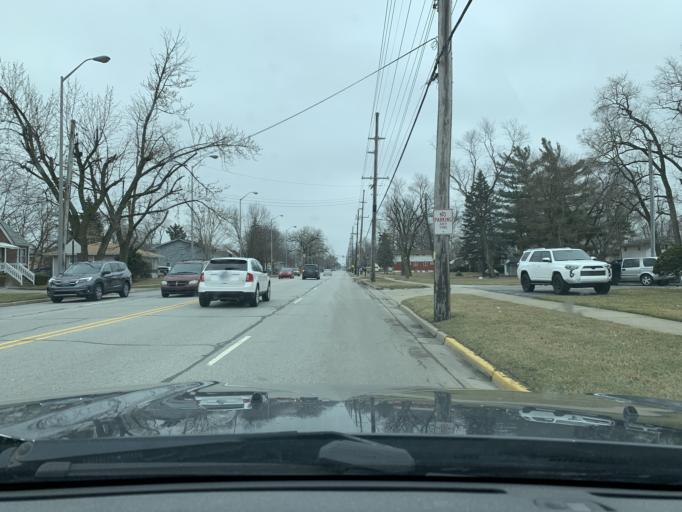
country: US
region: Indiana
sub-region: Lake County
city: Highland
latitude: 41.5464
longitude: -87.4616
